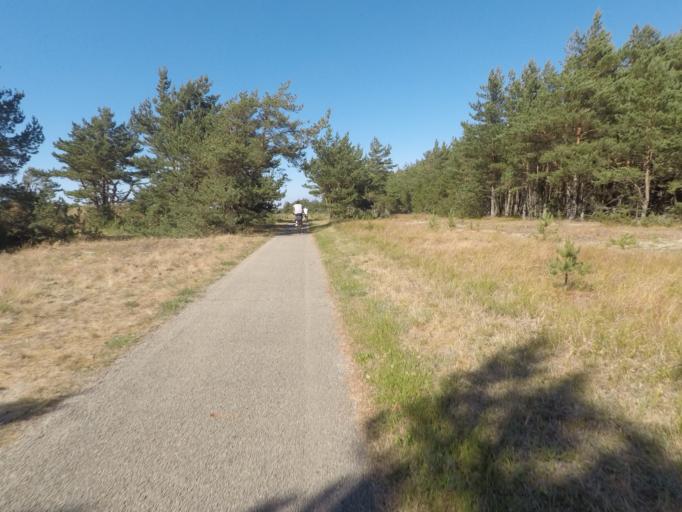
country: LT
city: Neringa
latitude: 55.4976
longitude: 21.0884
